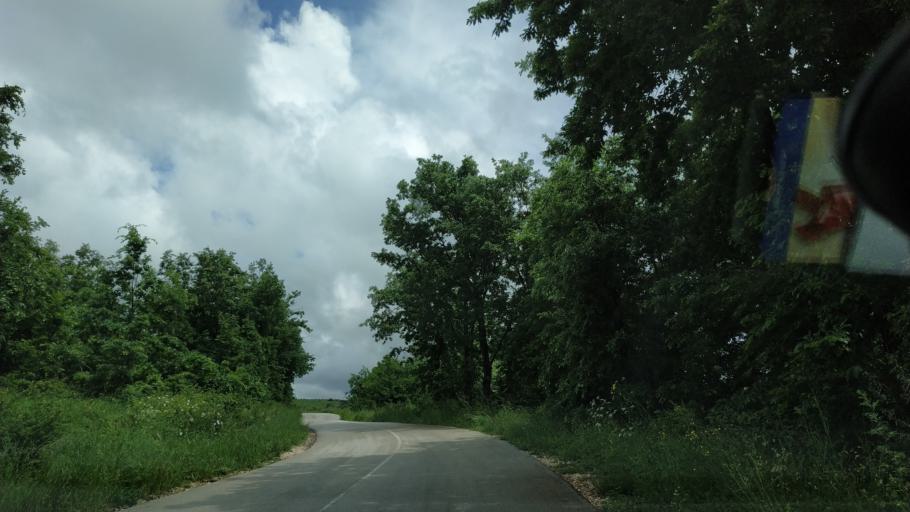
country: RS
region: Central Serbia
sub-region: Zajecarski Okrug
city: Soko Banja
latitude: 43.6878
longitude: 21.9328
